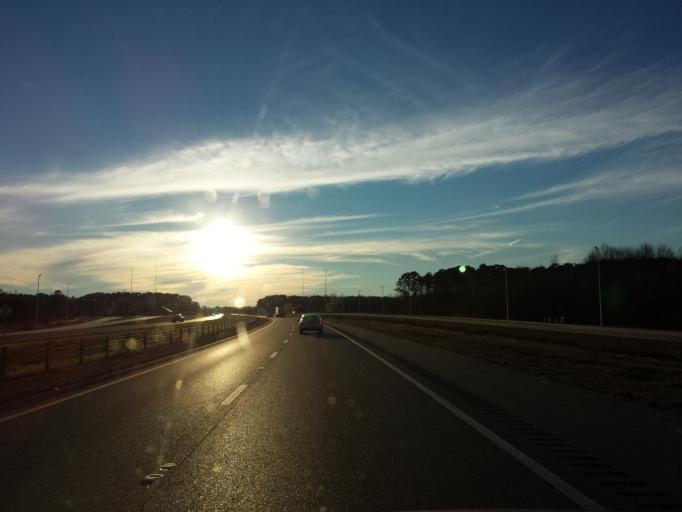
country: US
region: Alabama
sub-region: Sumter County
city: York
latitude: 32.4404
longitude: -88.4312
